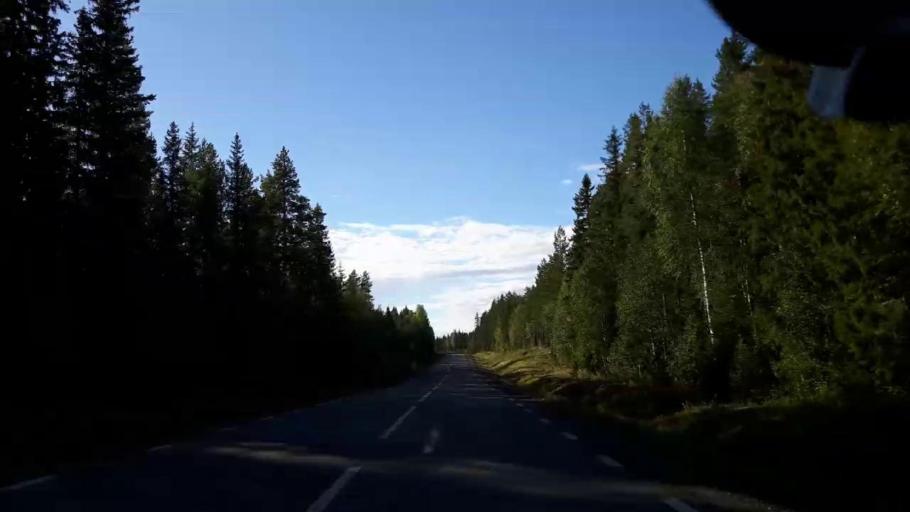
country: SE
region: Jaemtland
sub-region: Ragunda Kommun
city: Hammarstrand
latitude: 63.5341
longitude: 16.0452
